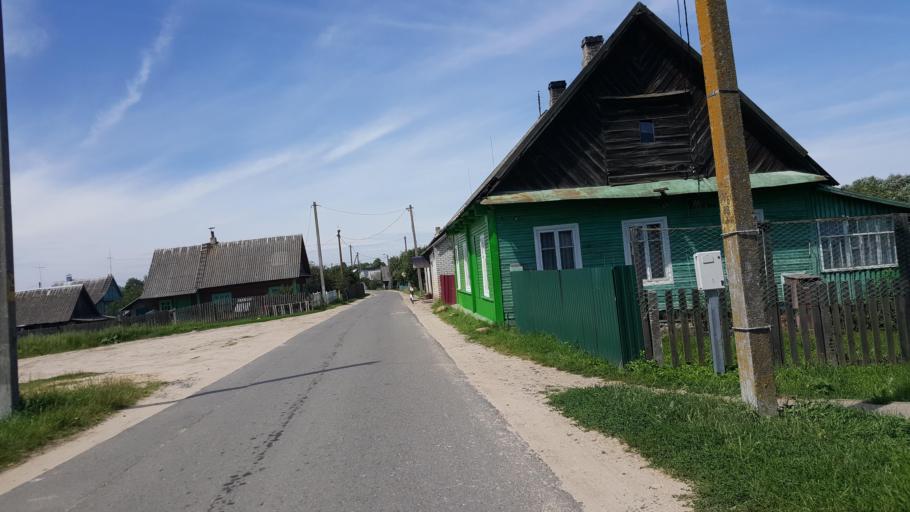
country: BY
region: Brest
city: Pruzhany
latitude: 52.5554
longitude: 24.2136
